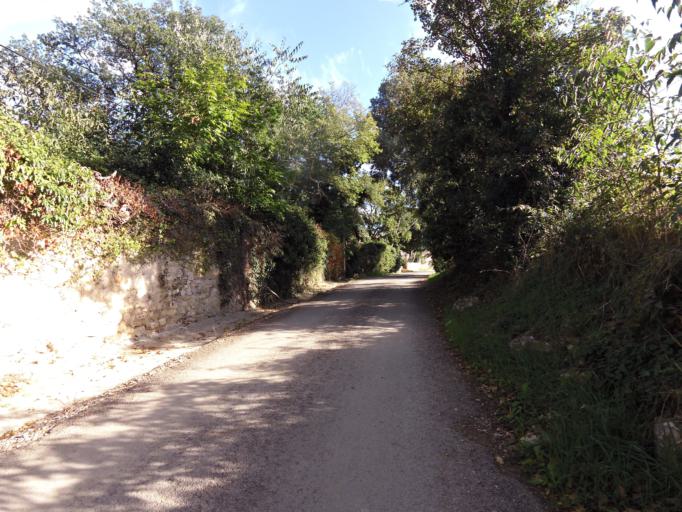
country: FR
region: Languedoc-Roussillon
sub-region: Departement du Gard
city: Villevieille
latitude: 43.8083
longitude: 4.0886
